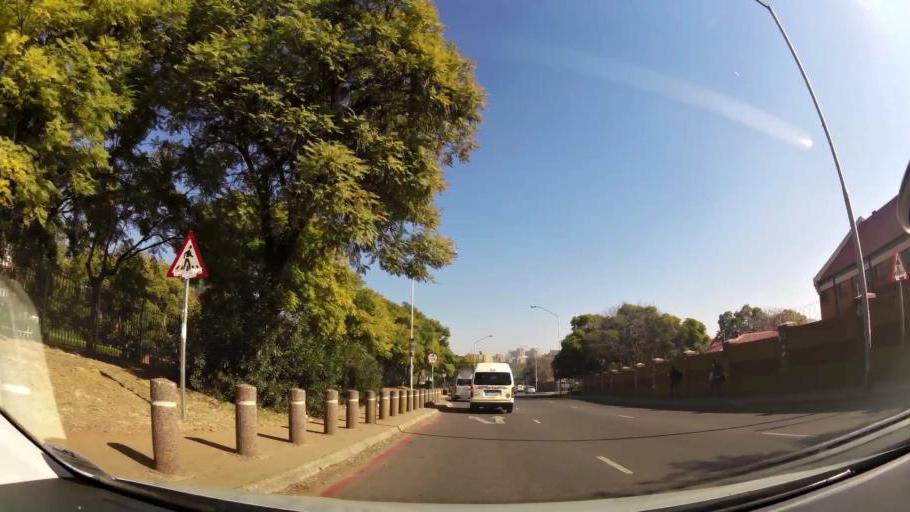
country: ZA
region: Gauteng
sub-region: City of Tshwane Metropolitan Municipality
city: Pretoria
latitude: -25.7580
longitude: 28.1992
